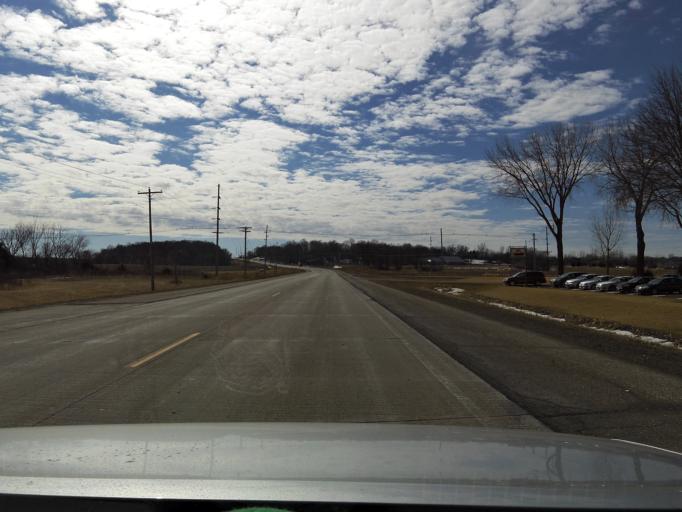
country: US
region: Minnesota
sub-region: Le Sueur County
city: New Prague
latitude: 44.5377
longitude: -93.5846
